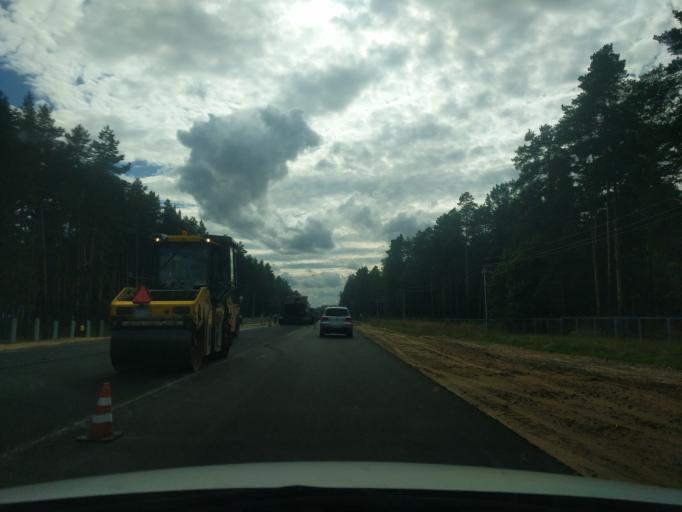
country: RU
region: Jaroslavl
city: Levashevo
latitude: 57.6773
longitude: 40.5904
